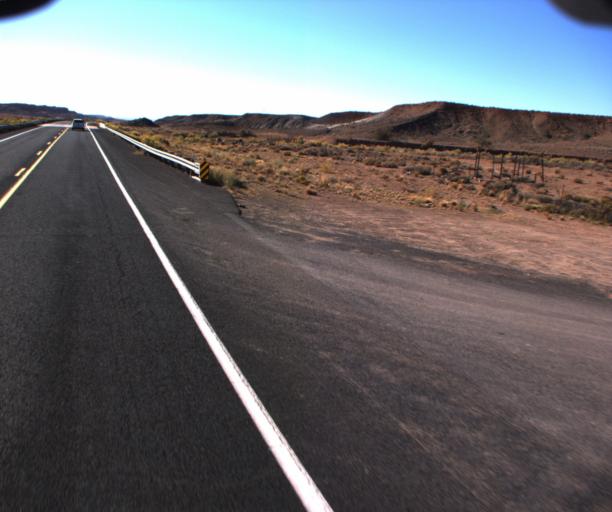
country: US
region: Arizona
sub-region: Coconino County
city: Tuba City
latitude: 36.2106
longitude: -111.3945
